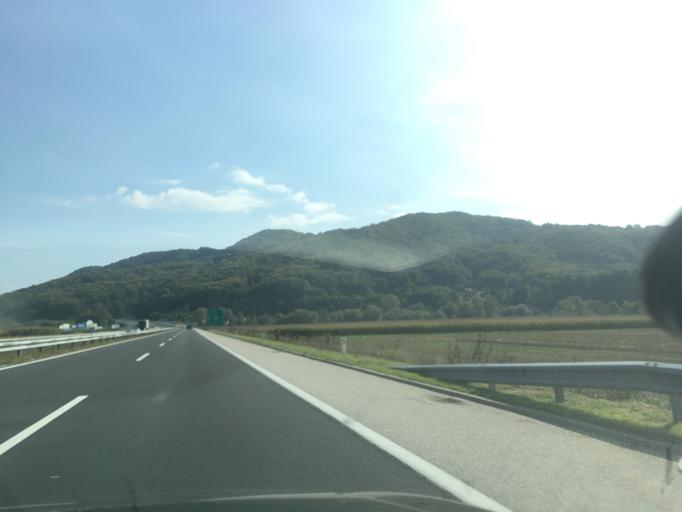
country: SI
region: Brezice
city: Brezice
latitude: 45.8972
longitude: 15.5794
